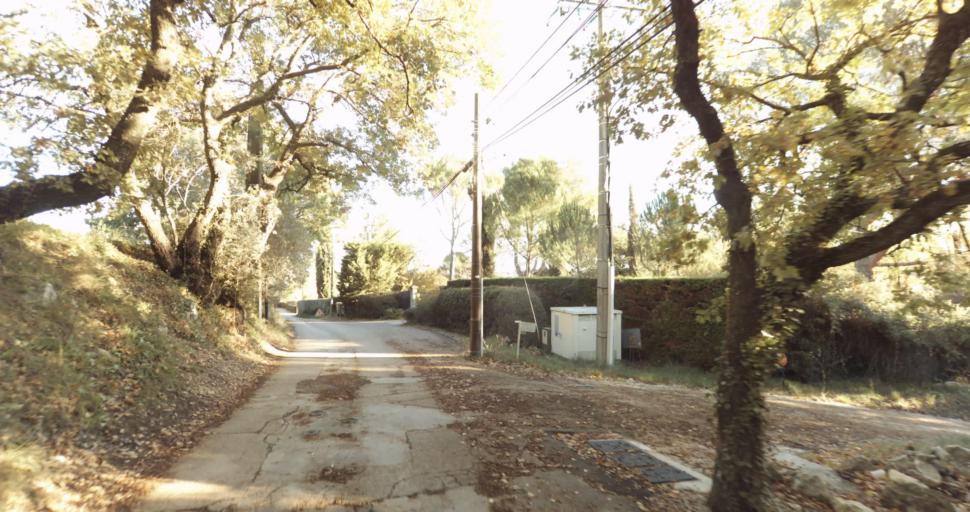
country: FR
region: Provence-Alpes-Cote d'Azur
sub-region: Departement des Bouches-du-Rhone
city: Venelles
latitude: 43.6060
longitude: 5.4816
